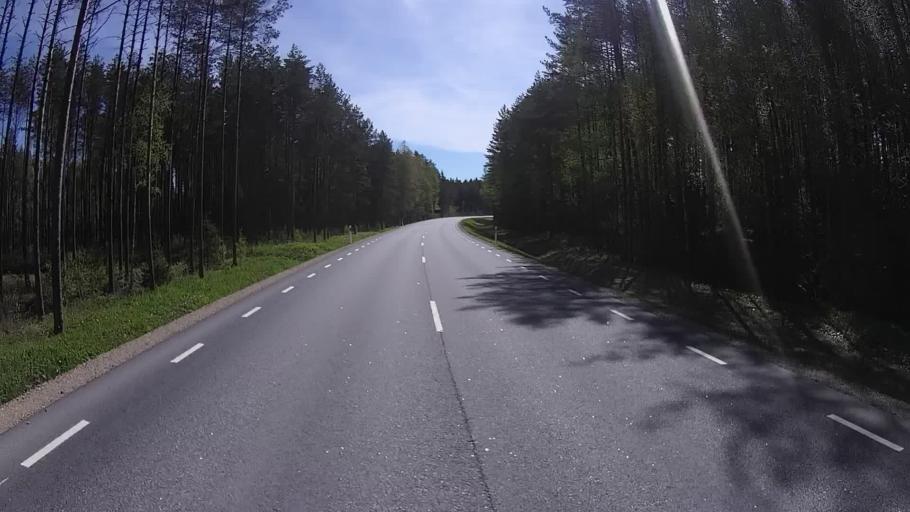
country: EE
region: Polvamaa
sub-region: Raepina vald
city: Rapina
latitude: 57.9681
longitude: 27.4411
